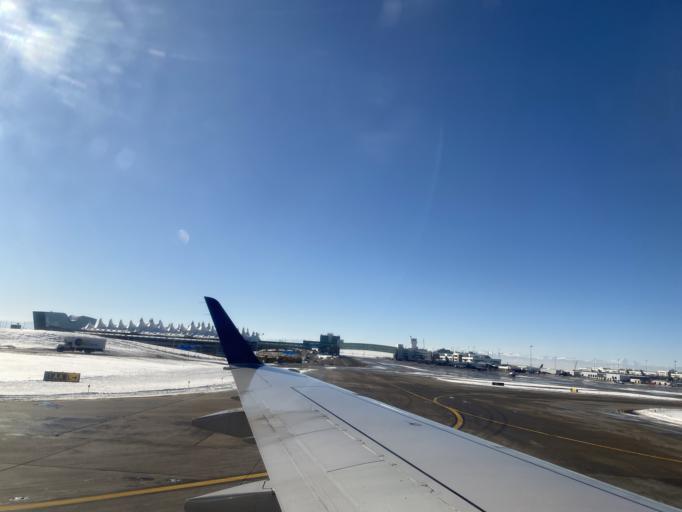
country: US
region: Colorado
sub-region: Weld County
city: Lochbuie
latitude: 39.8518
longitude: -104.6624
